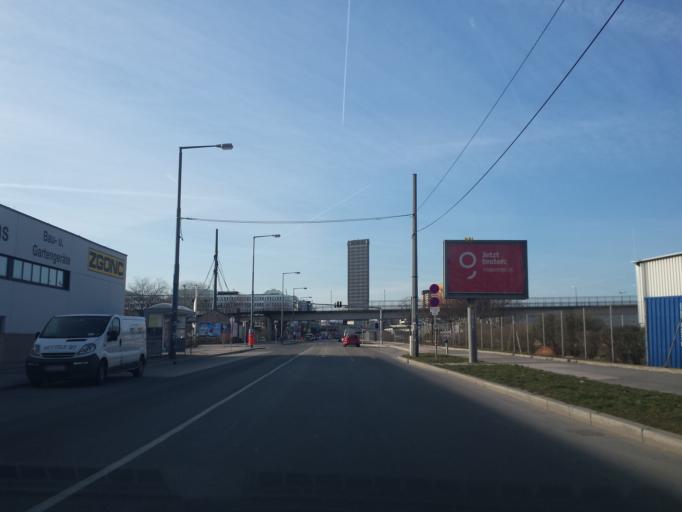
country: AT
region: Vienna
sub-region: Wien Stadt
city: Vienna
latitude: 48.1881
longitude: 16.4191
